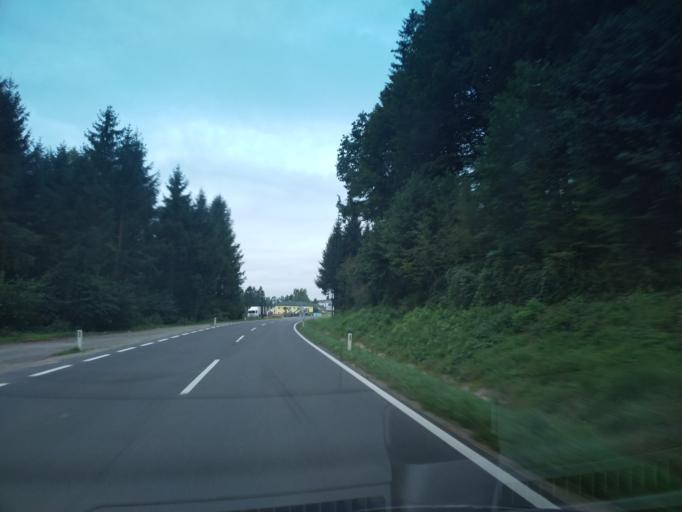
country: AT
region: Styria
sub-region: Politischer Bezirk Deutschlandsberg
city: Pitschgau
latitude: 46.7065
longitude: 15.2483
